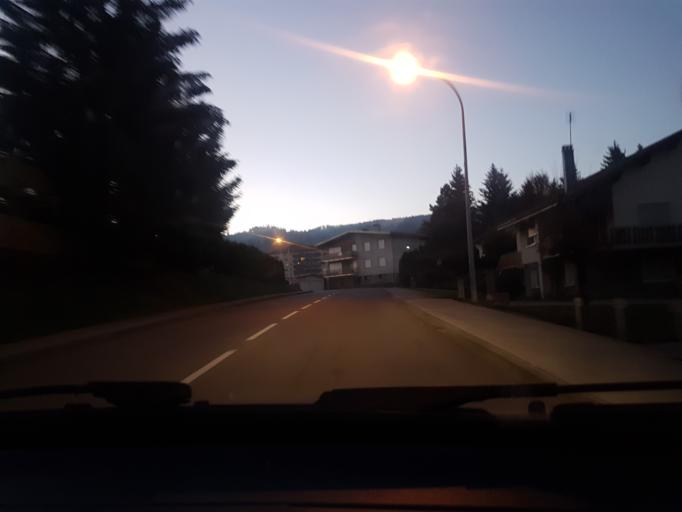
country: FR
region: Franche-Comte
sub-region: Departement du Doubs
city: Morteau
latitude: 47.0571
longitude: 6.6132
